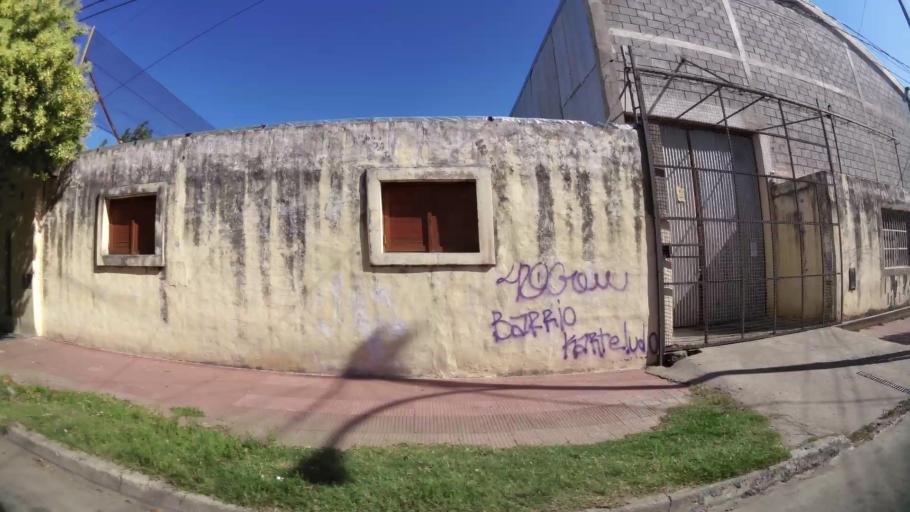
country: AR
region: Cordoba
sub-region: Departamento de Capital
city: Cordoba
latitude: -31.4138
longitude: -64.1577
